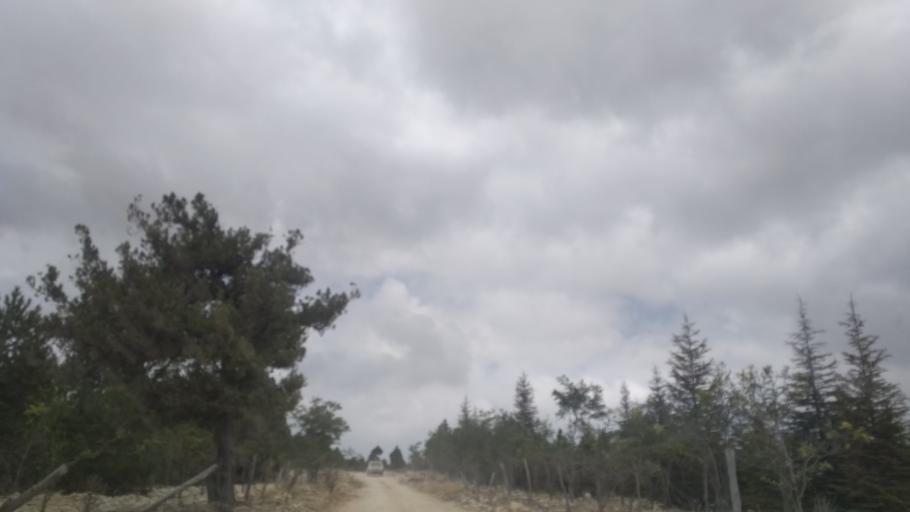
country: TR
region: Mersin
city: Sarikavak
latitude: 36.5717
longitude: 33.7628
